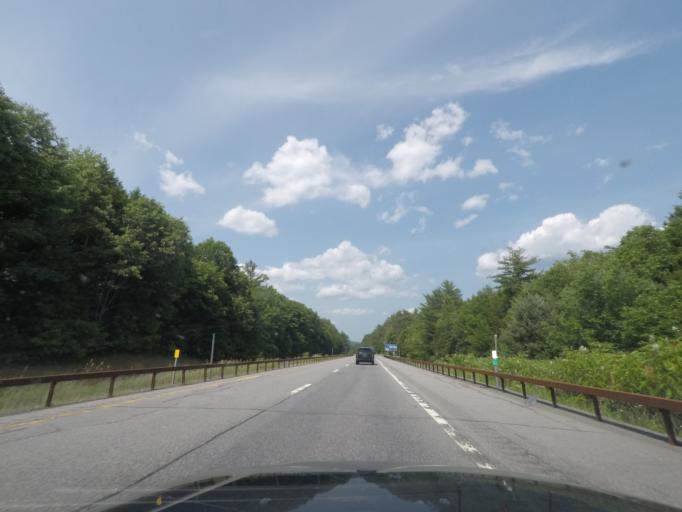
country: US
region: New York
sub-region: Essex County
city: Ticonderoga
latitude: 43.8563
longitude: -73.7605
